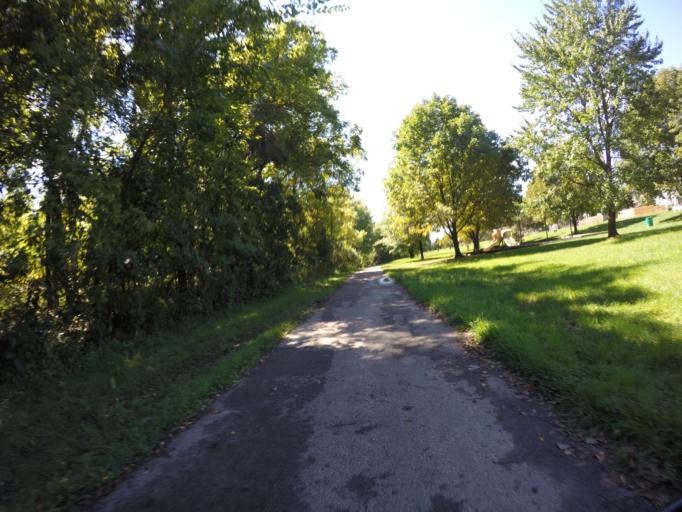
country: US
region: Kansas
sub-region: Johnson County
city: Lenexa
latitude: 38.9183
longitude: -94.7087
